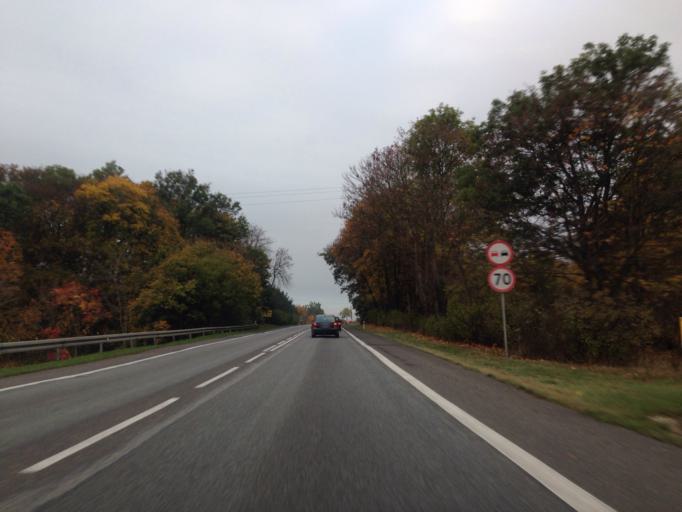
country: PL
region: Kujawsko-Pomorskie
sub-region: Powiat swiecki
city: Jezewo
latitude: 53.4325
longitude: 18.5323
